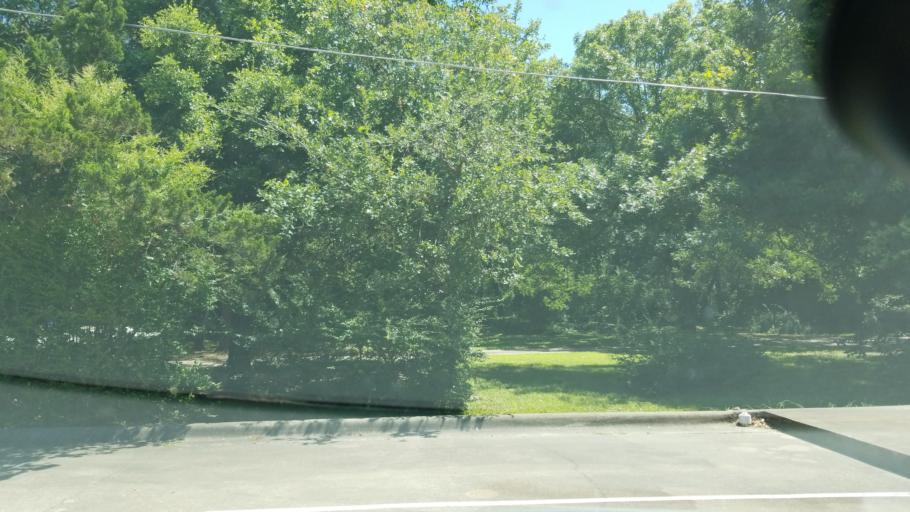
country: US
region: Texas
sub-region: Dallas County
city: Irving
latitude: 32.8319
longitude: -96.9595
